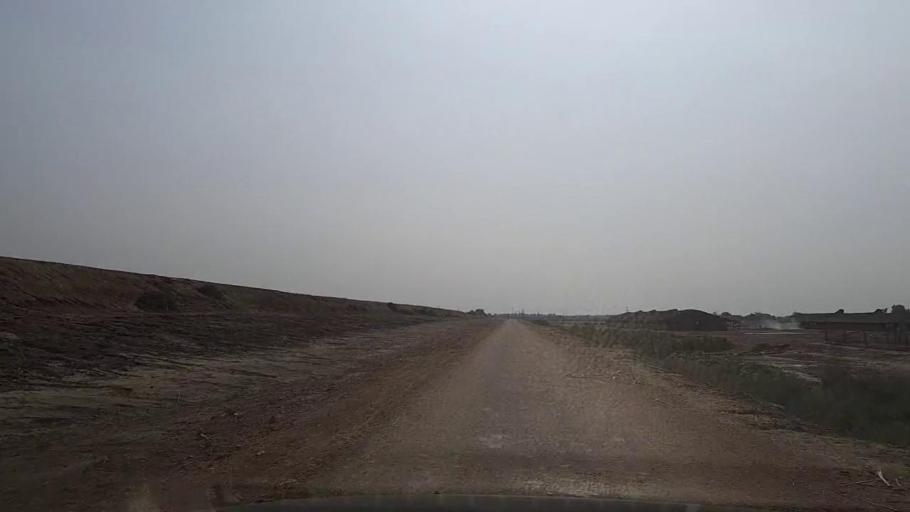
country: PK
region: Sindh
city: Thatta
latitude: 24.5672
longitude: 67.9133
